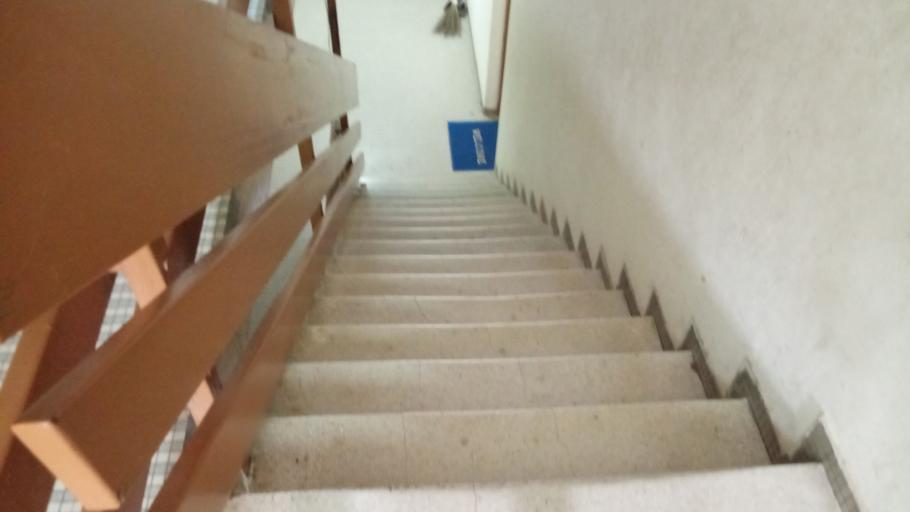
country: CI
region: Lagunes
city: Abidjan
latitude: 5.3346
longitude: -4.0019
